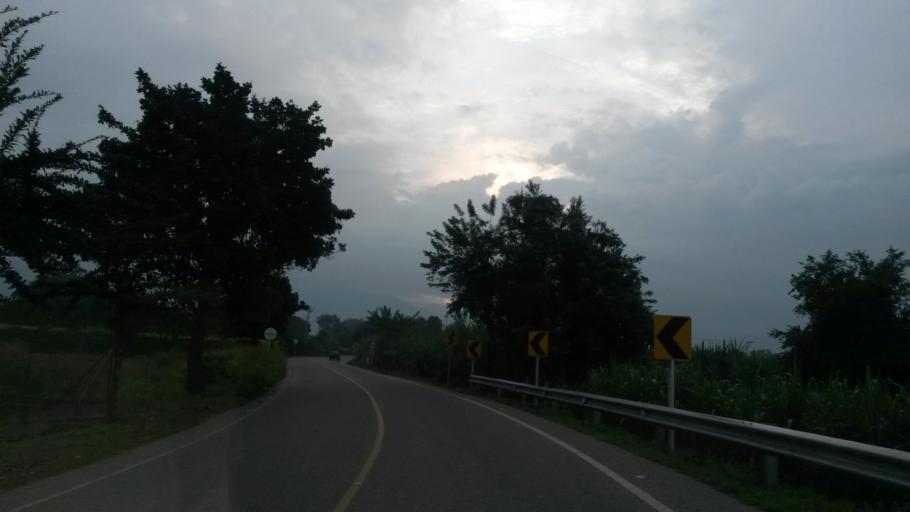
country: CO
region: Cauca
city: Padilla
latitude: 3.2285
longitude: -76.3219
